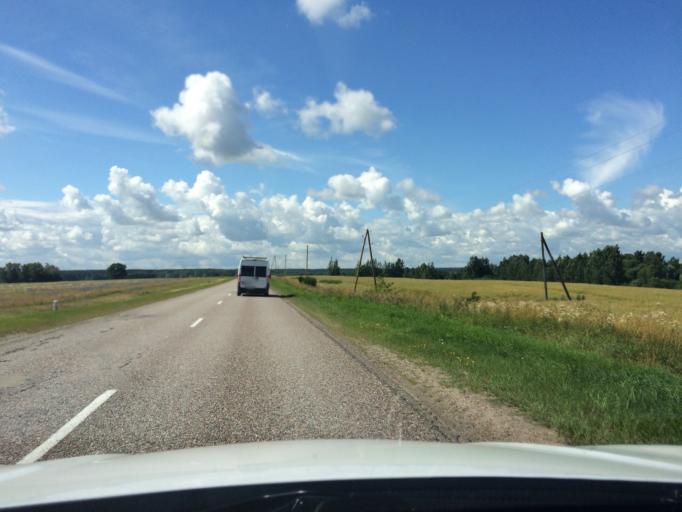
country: LV
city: Tervete
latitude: 56.5068
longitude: 23.4640
